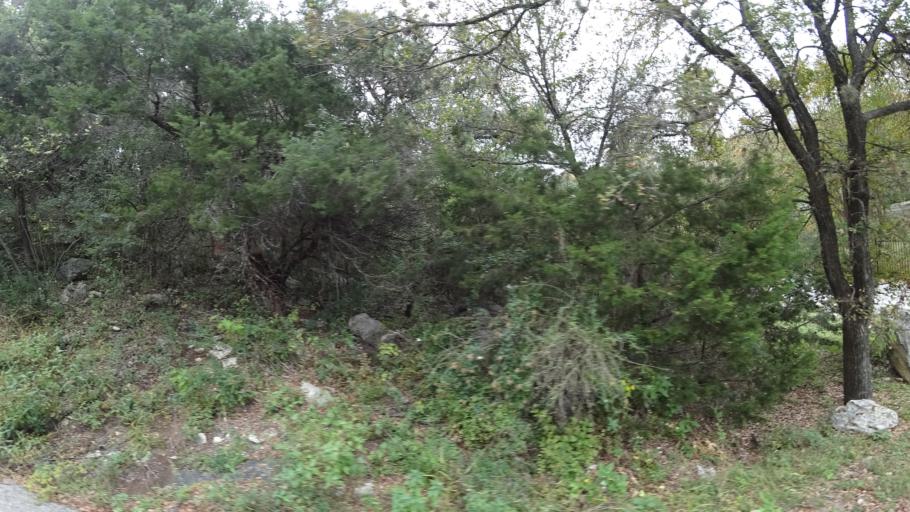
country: US
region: Texas
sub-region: Travis County
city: Bee Cave
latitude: 30.3434
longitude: -97.9307
